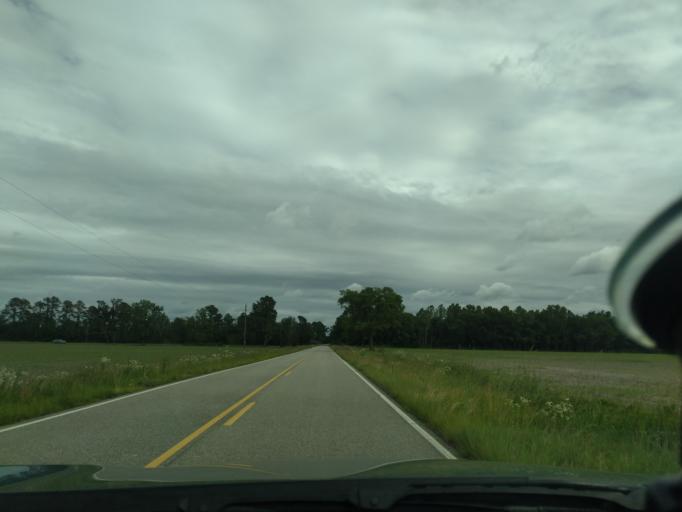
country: US
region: North Carolina
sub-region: Washington County
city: Plymouth
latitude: 35.8762
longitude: -76.7065
